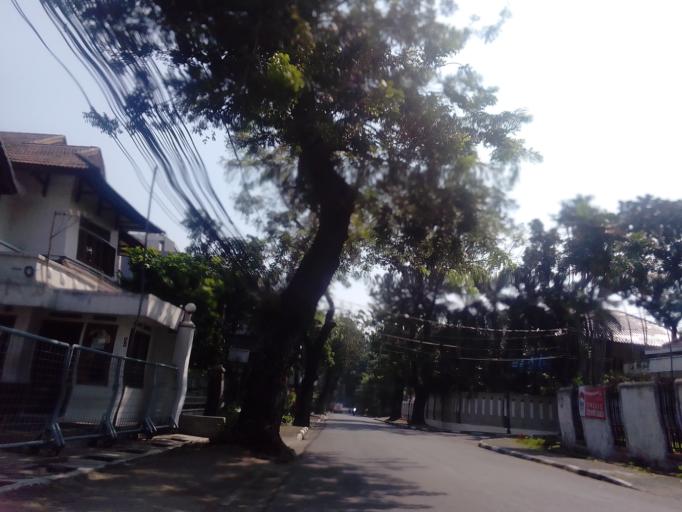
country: ID
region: Jakarta Raya
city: Jakarta
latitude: -6.2490
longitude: 106.7982
